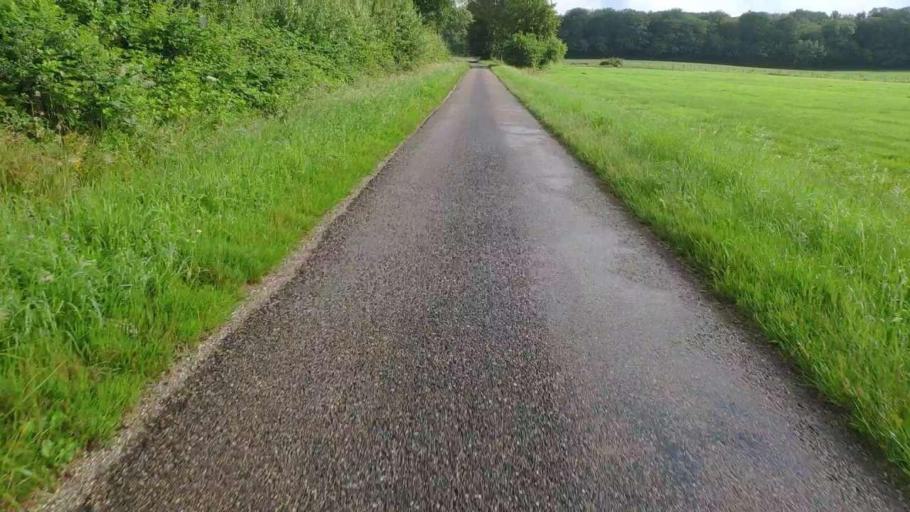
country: FR
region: Franche-Comte
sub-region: Departement du Jura
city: Mont-sous-Vaudrey
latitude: 46.8774
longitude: 5.5220
